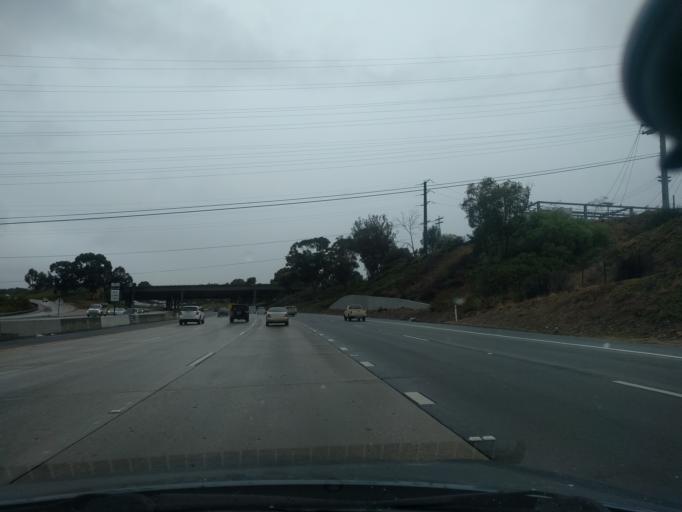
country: US
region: California
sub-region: San Diego County
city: San Diego
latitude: 32.7293
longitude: -117.1117
